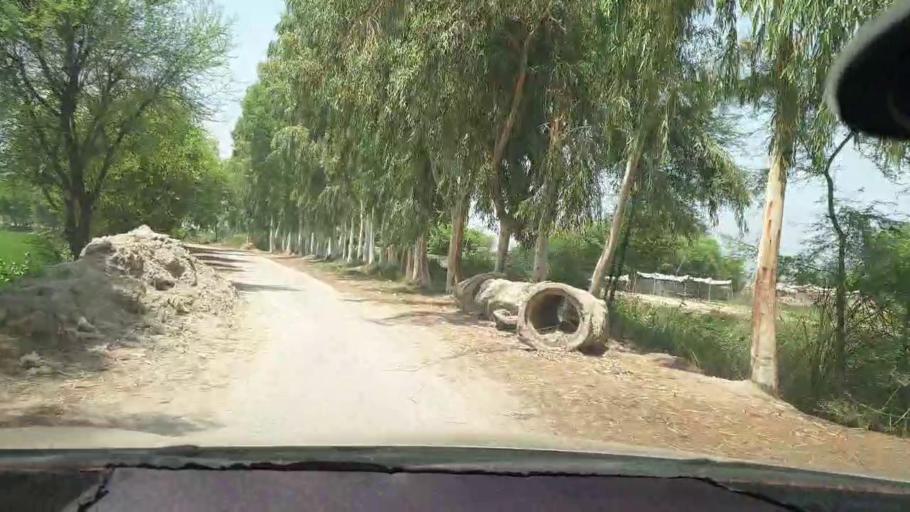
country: PK
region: Sindh
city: Kambar
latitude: 27.6636
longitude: 67.9264
